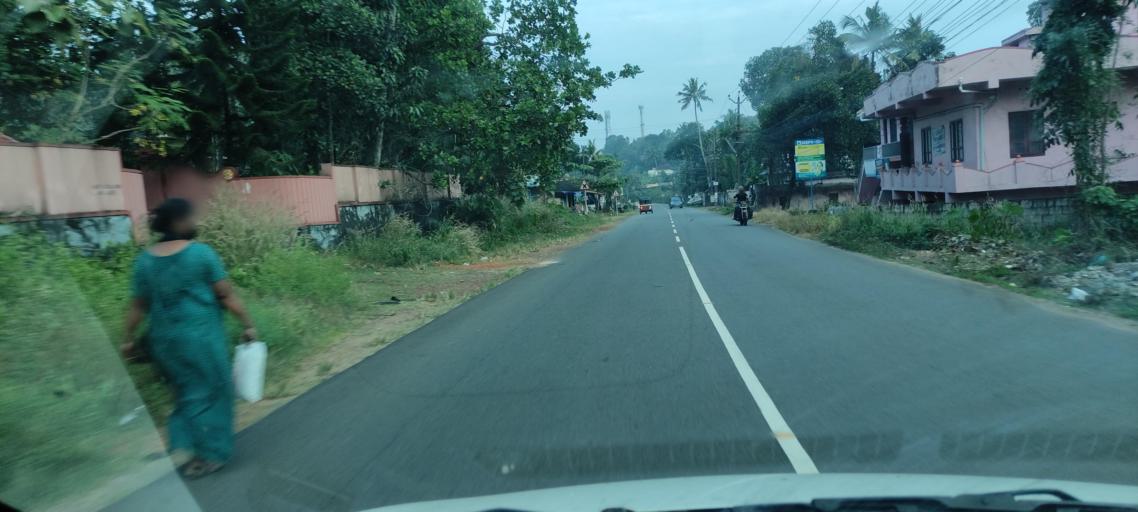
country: IN
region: Kerala
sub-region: Pattanamtitta
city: Adur
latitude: 9.1321
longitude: 76.7129
